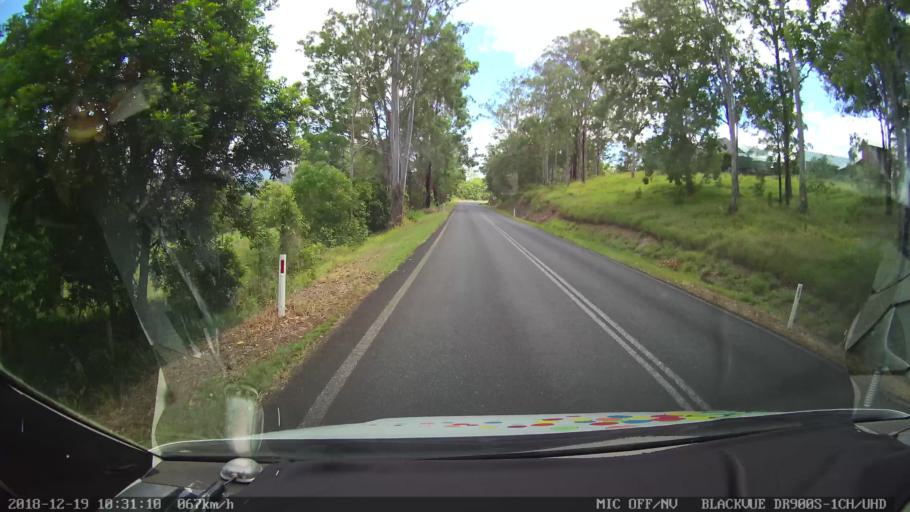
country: AU
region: New South Wales
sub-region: Lismore Municipality
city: Larnook
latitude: -28.5915
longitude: 153.1145
